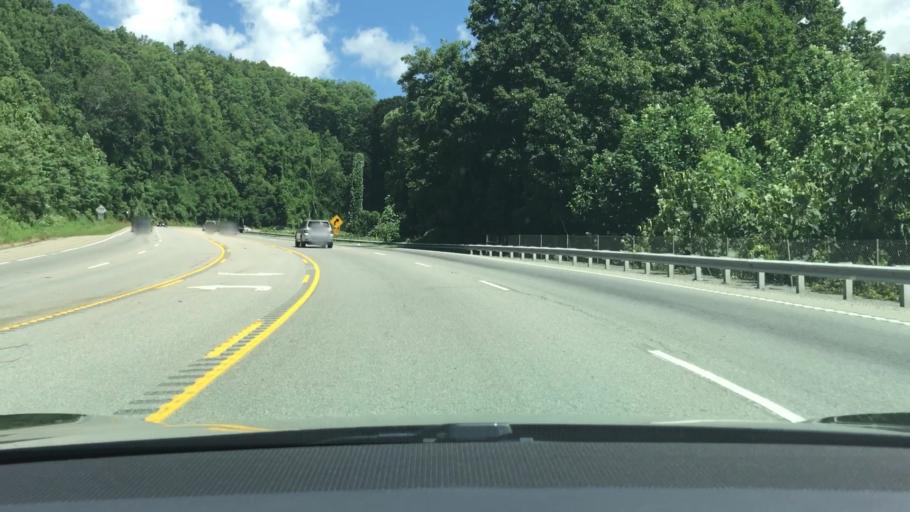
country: US
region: North Carolina
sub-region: Macon County
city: Franklin
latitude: 35.2527
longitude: -83.3161
